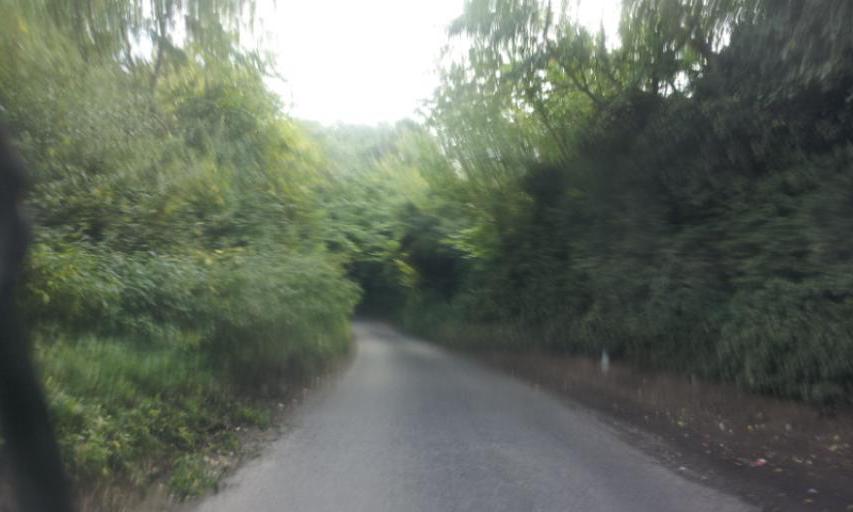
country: GB
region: England
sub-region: Kent
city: Newington
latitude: 51.3385
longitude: 0.6675
